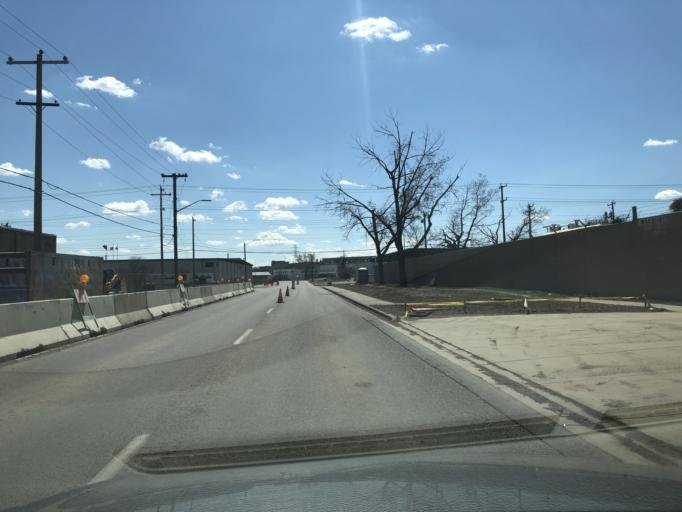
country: CA
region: Alberta
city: Calgary
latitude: 51.0241
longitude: -114.0310
